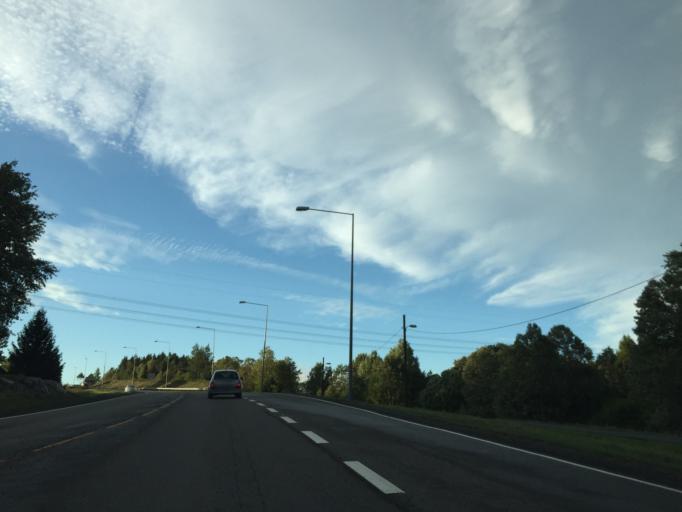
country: NO
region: Akershus
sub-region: Oppegard
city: Kolbotn
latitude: 59.8365
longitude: 10.8424
